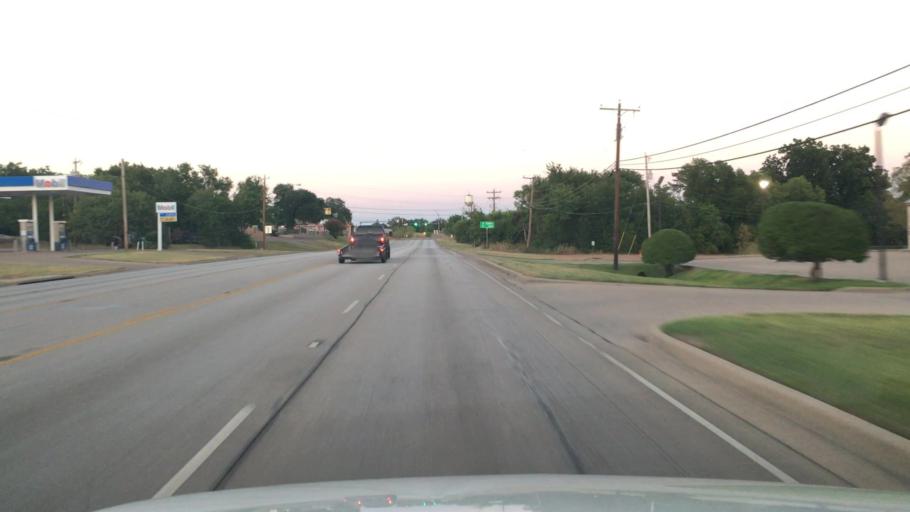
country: US
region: Texas
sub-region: Somervell County
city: Glen Rose
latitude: 32.2347
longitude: -97.7646
